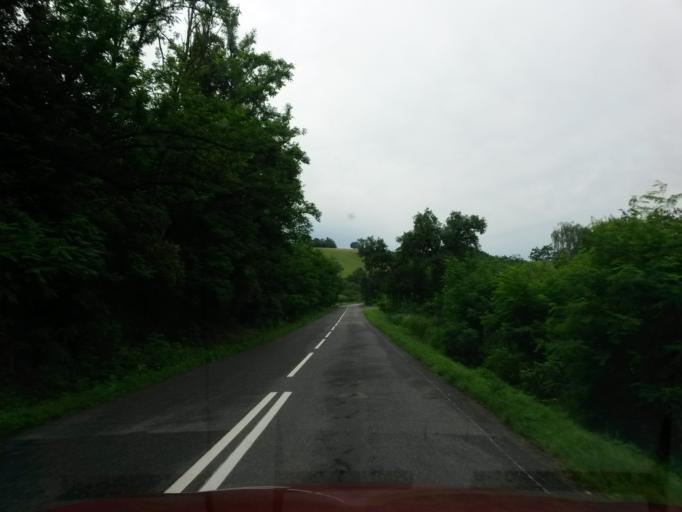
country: SK
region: Banskobystricky
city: Dudince
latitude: 48.1554
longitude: 18.9132
